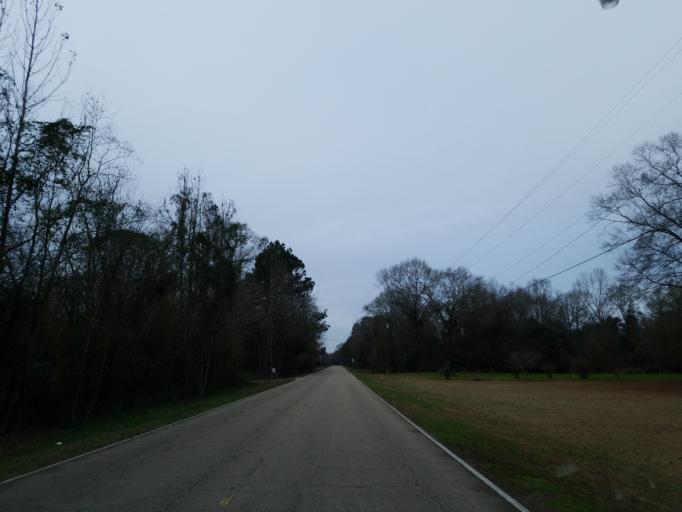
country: US
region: Mississippi
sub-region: Forrest County
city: Hattiesburg
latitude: 31.2836
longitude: -89.2547
